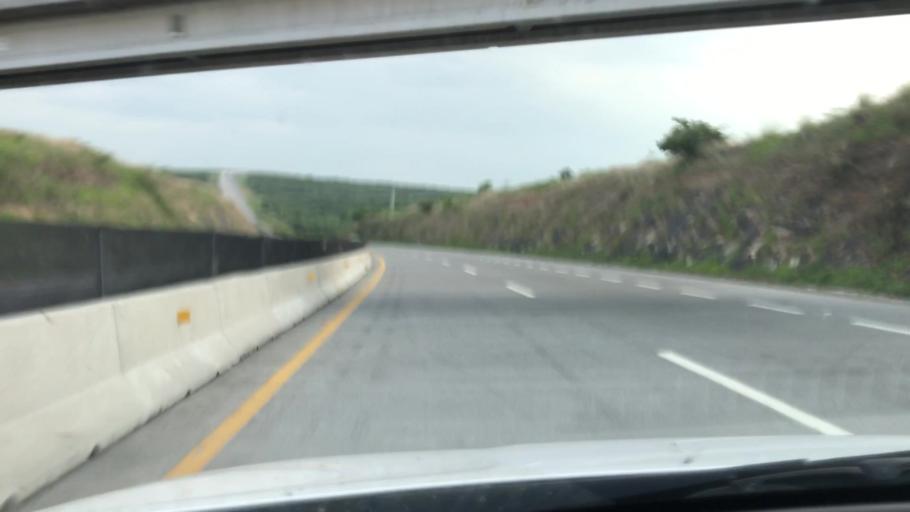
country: MX
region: Jalisco
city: Degollado
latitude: 20.3824
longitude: -102.1195
